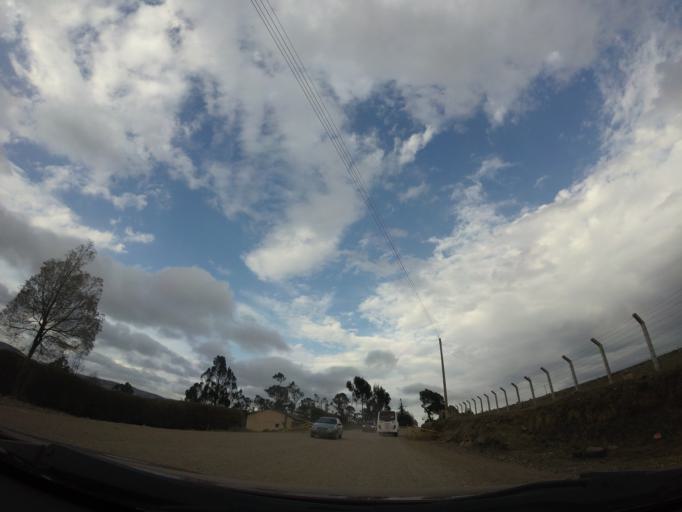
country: CO
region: Boyaca
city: Tunja
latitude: 5.5449
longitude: -73.3842
